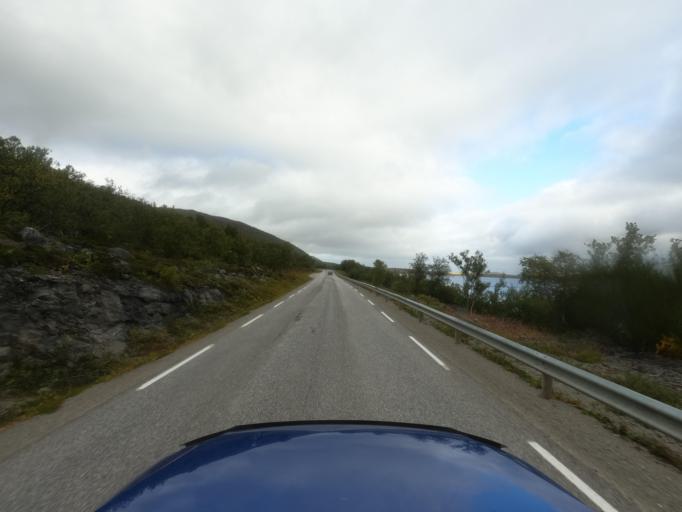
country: NO
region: Finnmark Fylke
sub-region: Porsanger
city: Lakselv
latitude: 70.3862
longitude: 25.1150
